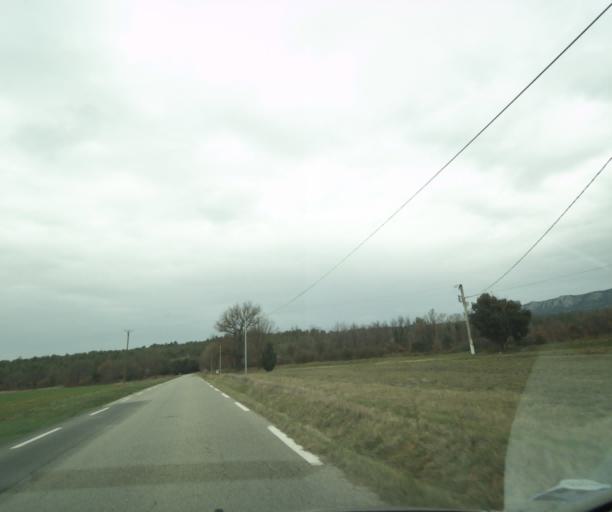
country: FR
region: Provence-Alpes-Cote d'Azur
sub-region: Departement des Bouches-du-Rhone
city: Jouques
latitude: 43.6203
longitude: 5.6769
